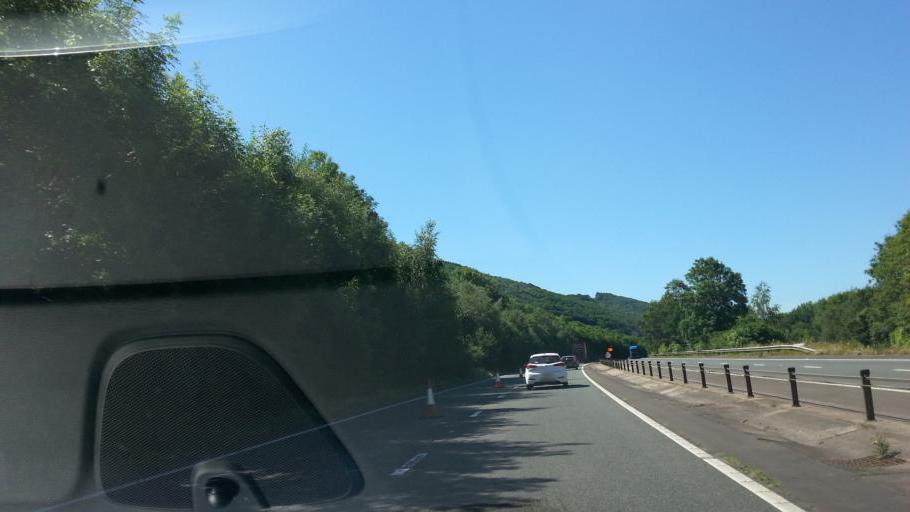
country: GB
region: Wales
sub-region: Monmouthshire
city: Llangybi
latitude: 51.6427
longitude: -2.8810
